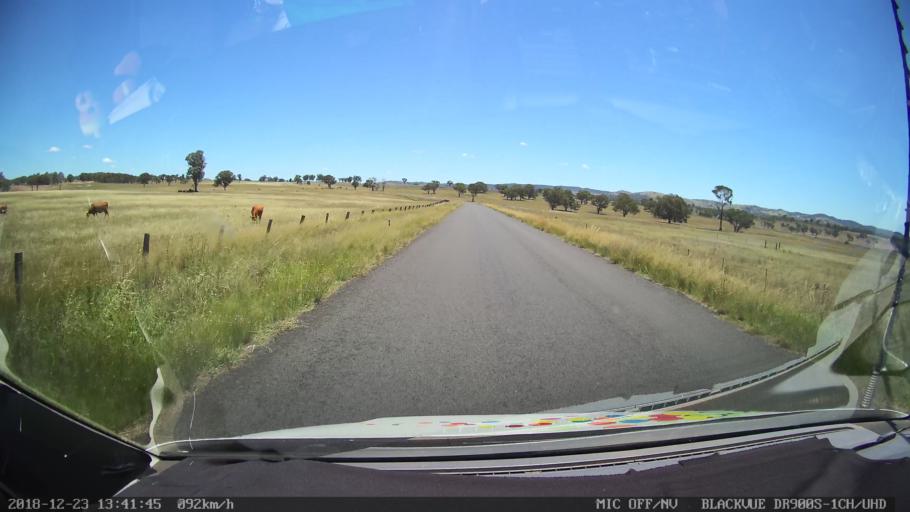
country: AU
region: New South Wales
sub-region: Armidale Dumaresq
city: Armidale
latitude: -30.4705
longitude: 151.1714
